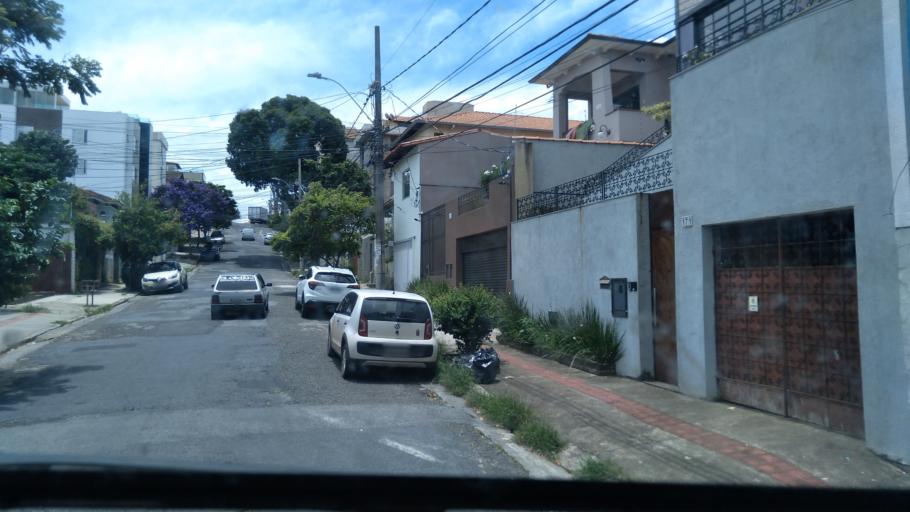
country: BR
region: Minas Gerais
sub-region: Belo Horizonte
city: Belo Horizonte
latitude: -19.9158
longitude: -43.9126
